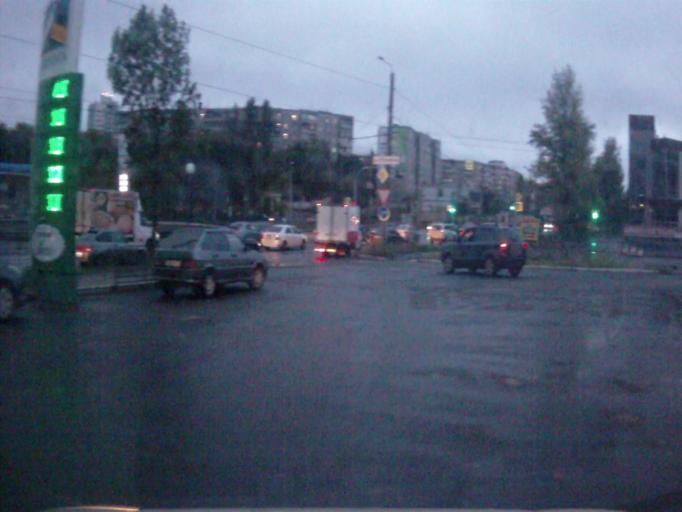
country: RU
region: Chelyabinsk
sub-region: Gorod Chelyabinsk
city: Chelyabinsk
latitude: 55.1399
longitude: 61.4592
